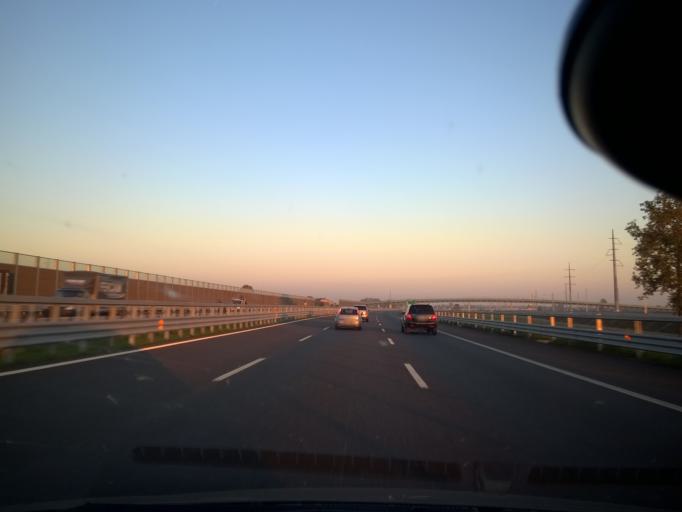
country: IT
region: Lombardy
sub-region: Provincia di Bergamo
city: Fornovo San Giovanni
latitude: 45.5106
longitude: 9.6770
